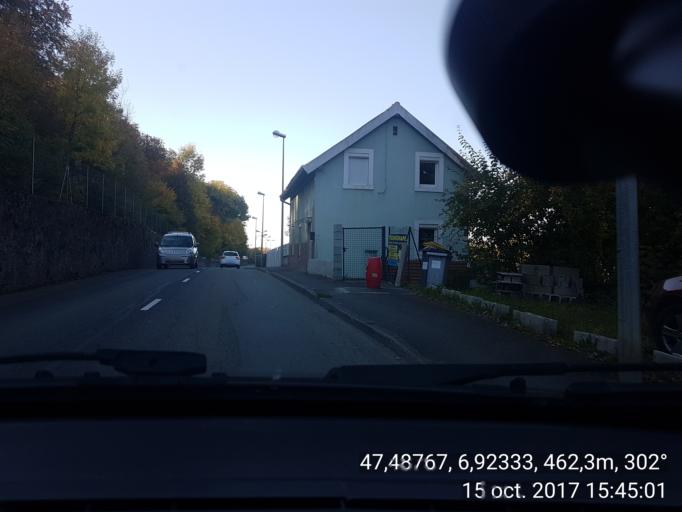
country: FR
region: Franche-Comte
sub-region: Territoire de Belfort
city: Beaucourt
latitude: 47.4877
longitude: 6.9234
